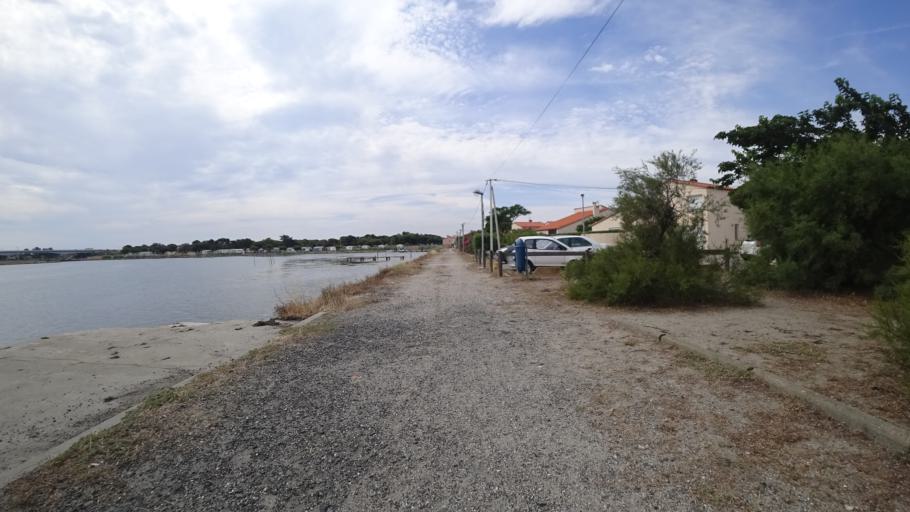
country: FR
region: Languedoc-Roussillon
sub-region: Departement des Pyrenees-Orientales
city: Le Barcares
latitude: 42.8077
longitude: 3.0271
